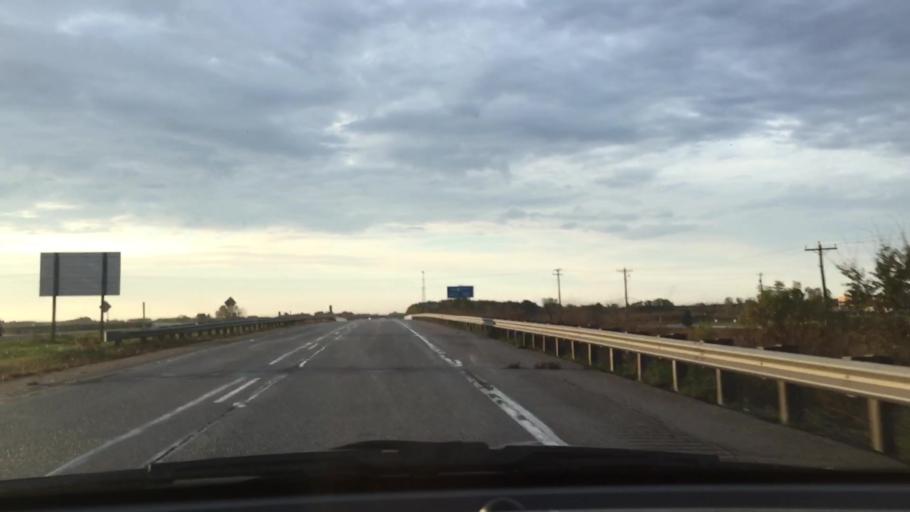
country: US
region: Wisconsin
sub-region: Walworth County
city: Elkhorn
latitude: 42.6842
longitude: -88.5289
